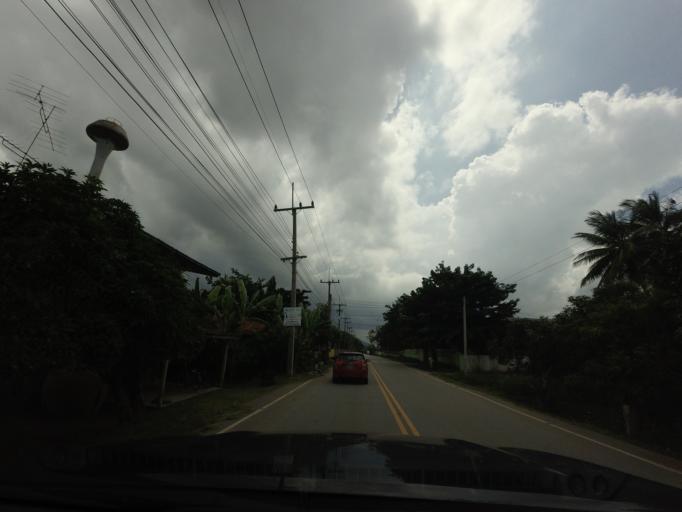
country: LA
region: Vientiane
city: Muang Sanakham
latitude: 18.0040
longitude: 101.7570
